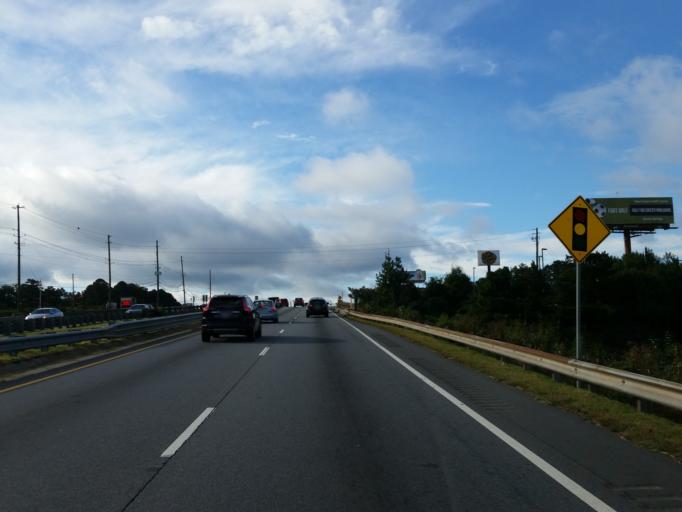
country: US
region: Georgia
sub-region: Cobb County
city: Kennesaw
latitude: 34.0128
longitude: -84.6120
